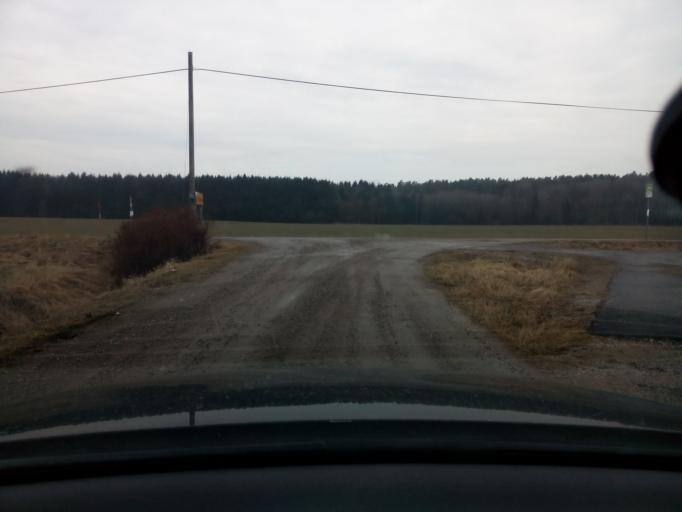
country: SE
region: Soedermanland
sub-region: Trosa Kommun
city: Vagnharad
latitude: 58.9300
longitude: 17.4275
